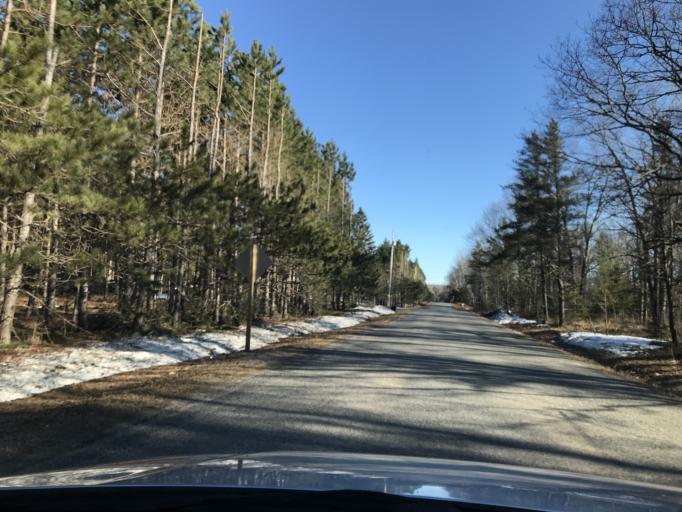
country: US
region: Wisconsin
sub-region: Marinette County
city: Peshtigo
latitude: 45.3583
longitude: -88.0296
